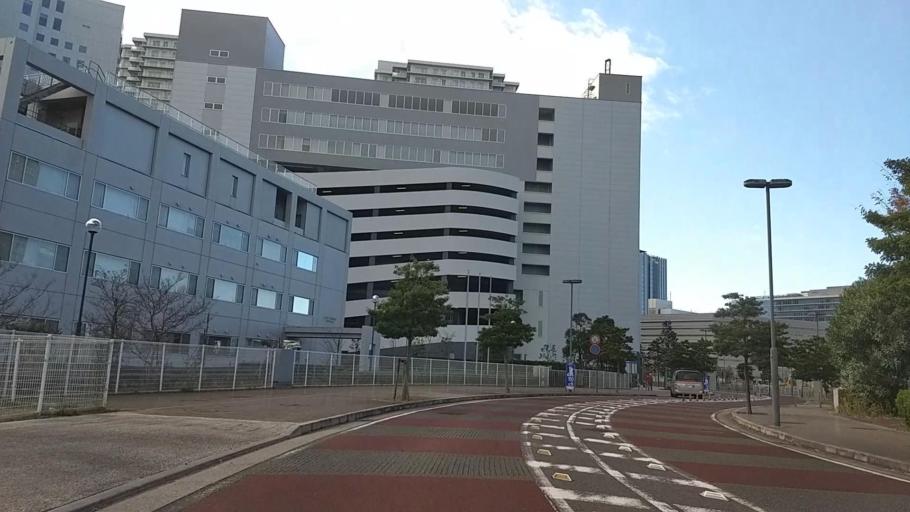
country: JP
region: Kanagawa
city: Yokohama
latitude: 35.4643
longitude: 139.6321
